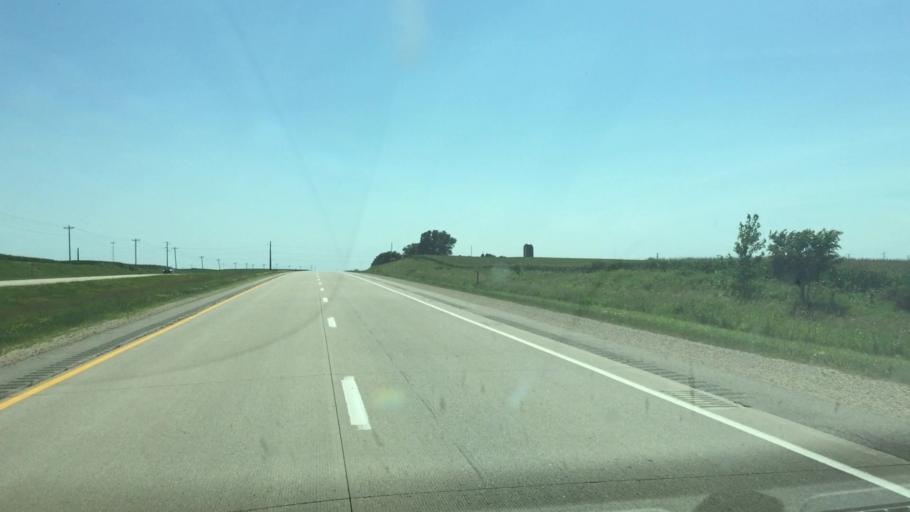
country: US
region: Iowa
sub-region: Dubuque County
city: Peosta
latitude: 42.3701
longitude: -90.7923
